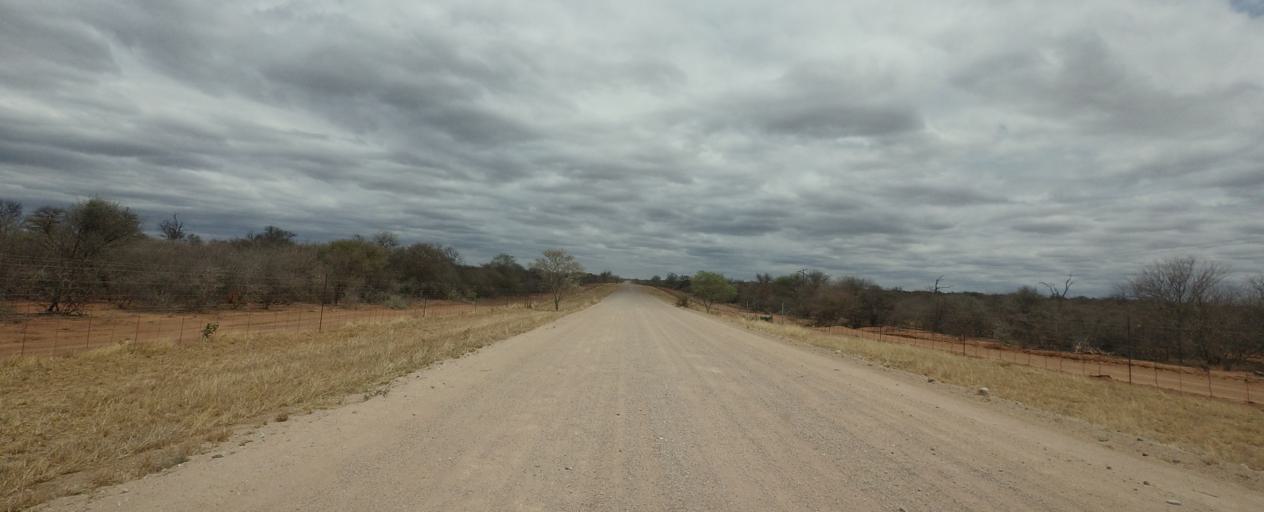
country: BW
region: Central
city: Mathathane
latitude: -22.6948
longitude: 28.6291
